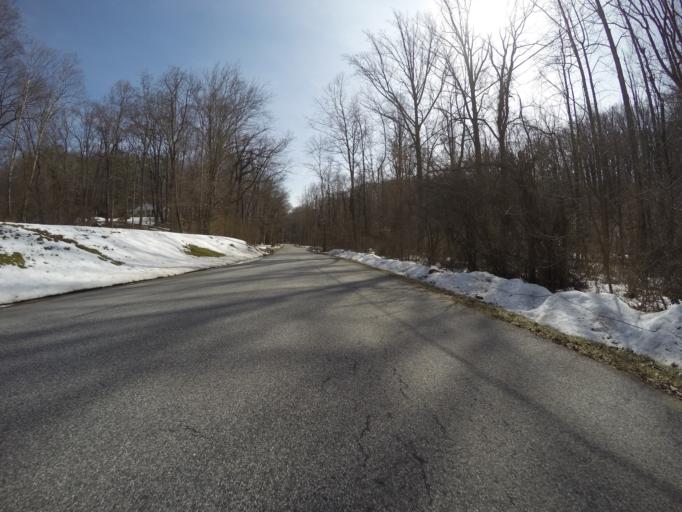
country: US
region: Maryland
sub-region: Baltimore County
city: Hunt Valley
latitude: 39.5046
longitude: -76.6536
